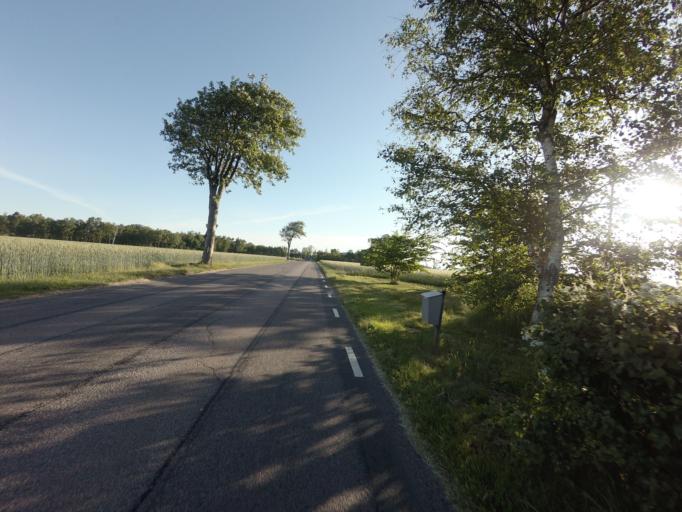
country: SE
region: Skane
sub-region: Hoganas Kommun
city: Hoganas
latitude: 56.2166
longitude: 12.6795
